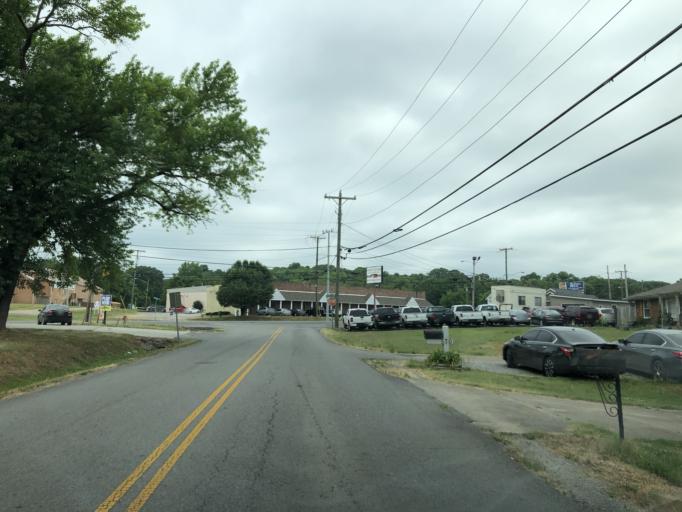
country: US
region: Tennessee
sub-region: Davidson County
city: Goodlettsville
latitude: 36.2918
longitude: -86.7338
